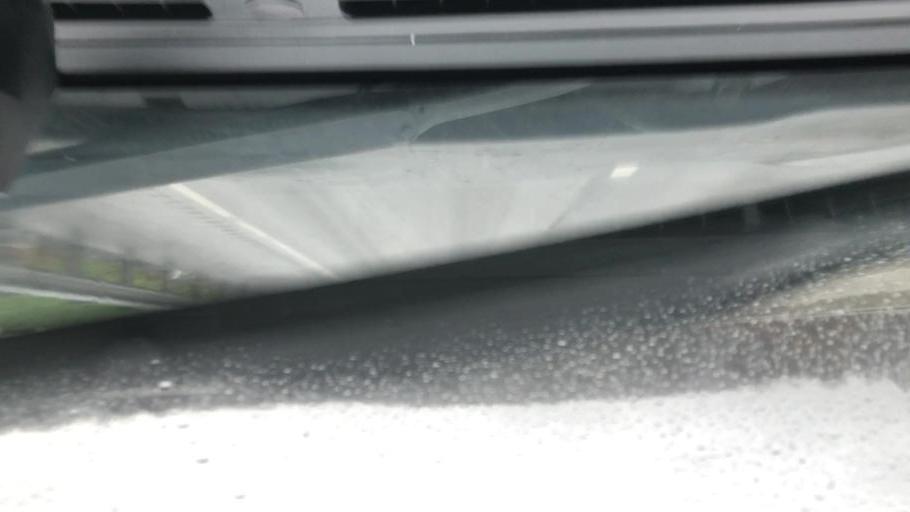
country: US
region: Pennsylvania
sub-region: Berks County
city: Boyertown
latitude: 40.3092
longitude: -75.6360
